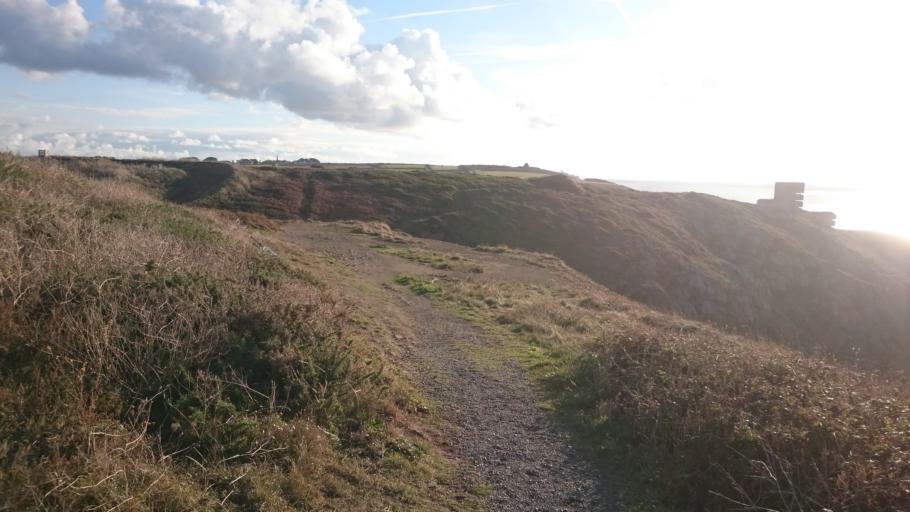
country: GG
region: St Peter Port
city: Saint Peter Port
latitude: 49.4262
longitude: -2.6667
